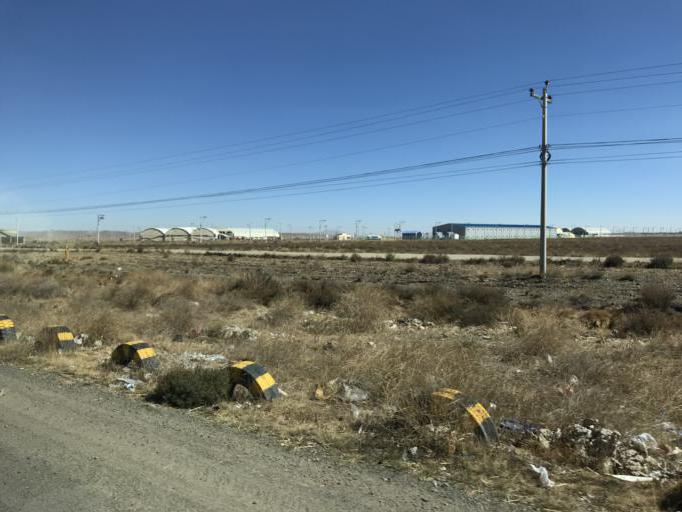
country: BO
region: La Paz
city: La Paz
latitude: -16.5207
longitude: -68.2946
